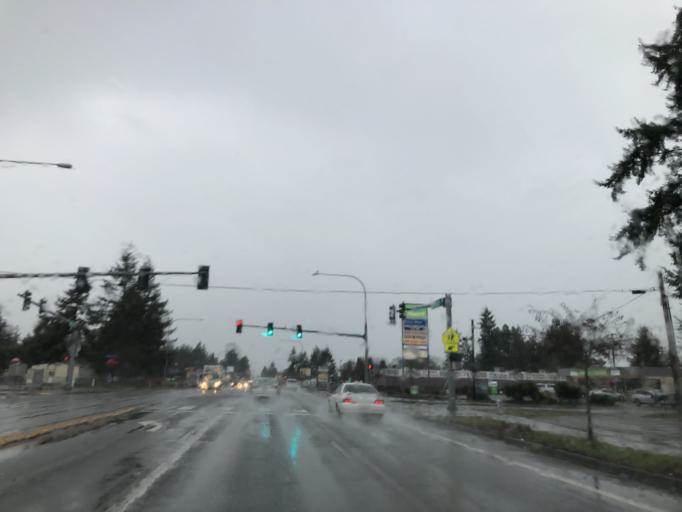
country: US
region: Washington
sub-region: Pierce County
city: Spanaway
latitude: 47.1059
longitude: -122.4347
